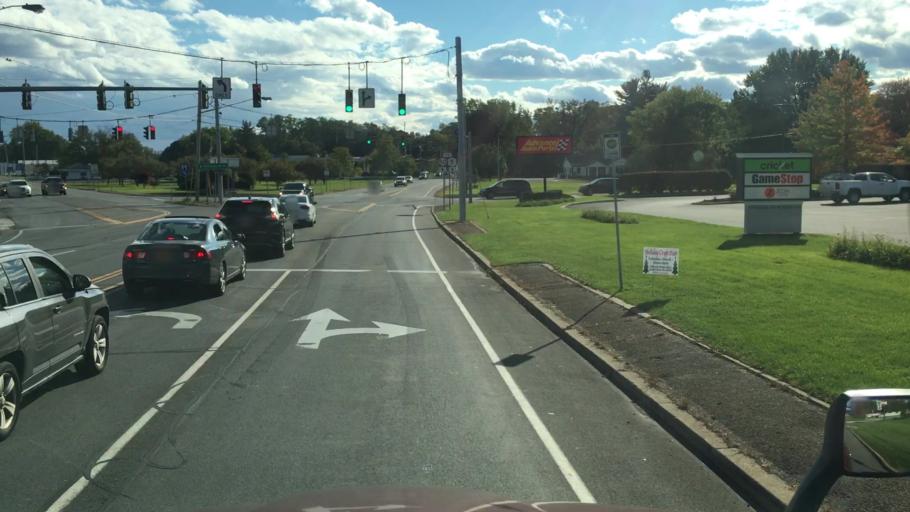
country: US
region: New York
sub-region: Schenectady County
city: Scotia
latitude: 42.8497
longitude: -73.9429
